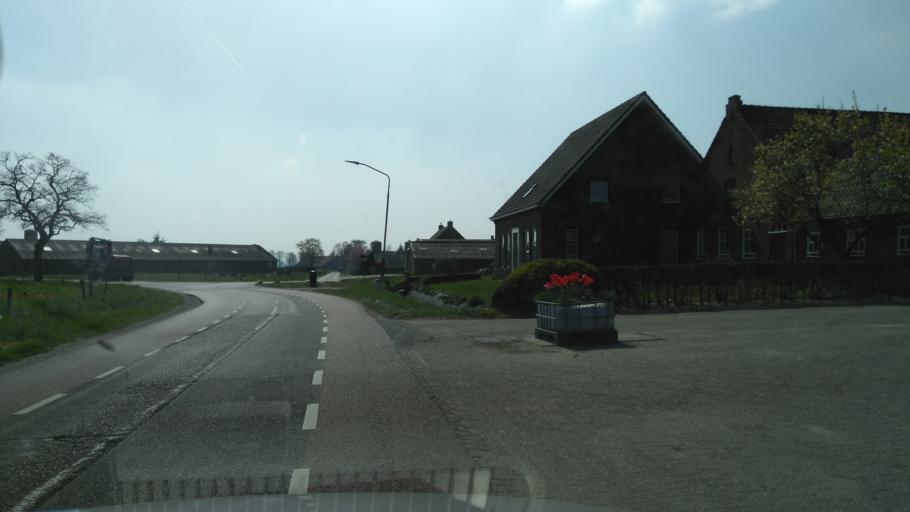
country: BE
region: Flanders
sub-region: Provincie Antwerpen
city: Baarle-Hertog
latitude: 51.4271
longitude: 4.9058
